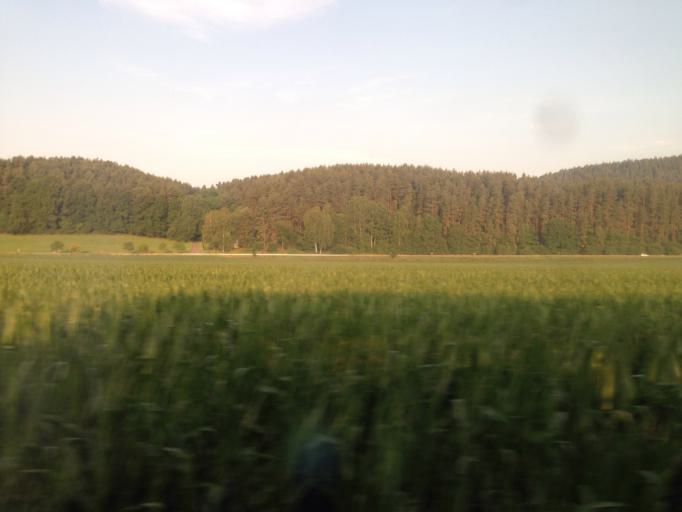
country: DE
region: Thuringia
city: Langenorla
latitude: 50.7194
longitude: 11.6072
